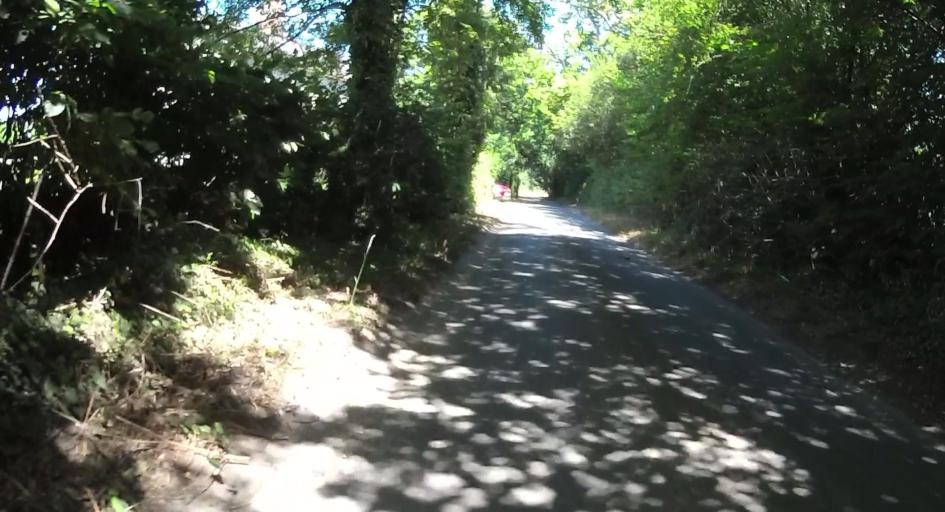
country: GB
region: England
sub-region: Dorset
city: Bovington Camp
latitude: 50.7024
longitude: -2.2866
